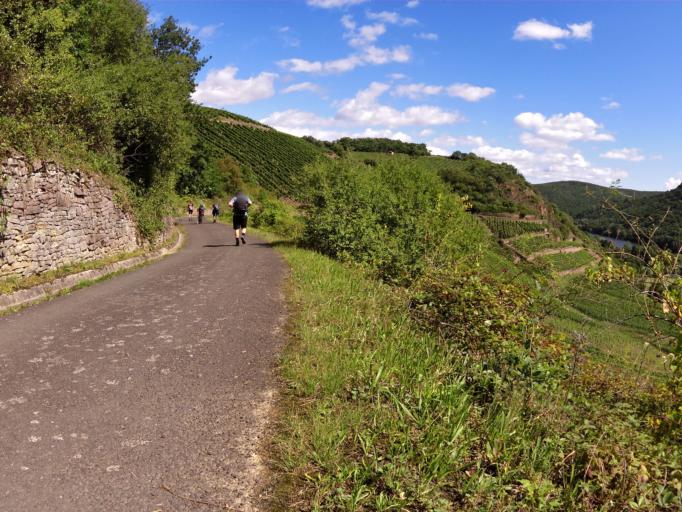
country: DE
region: Rheinland-Pfalz
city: Niederhausen
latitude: 49.7936
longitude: 7.7693
